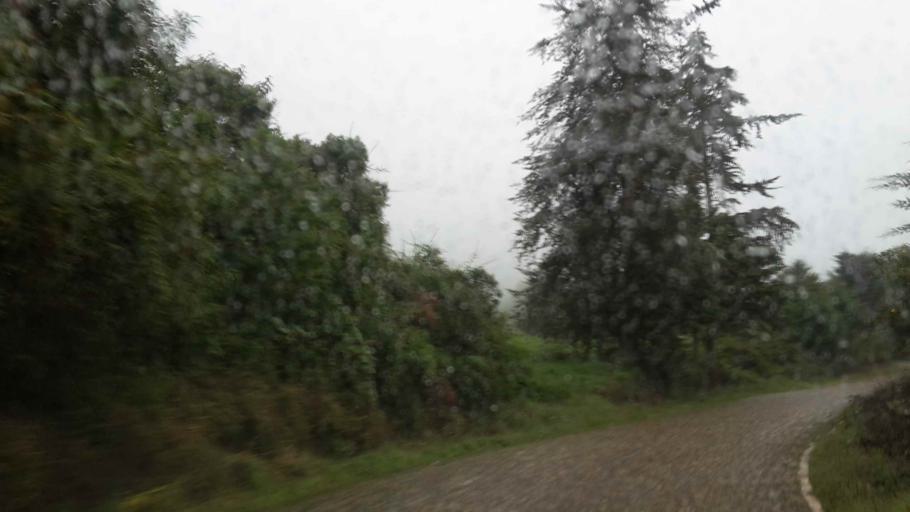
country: BO
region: Cochabamba
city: Colomi
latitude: -17.1481
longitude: -65.9142
